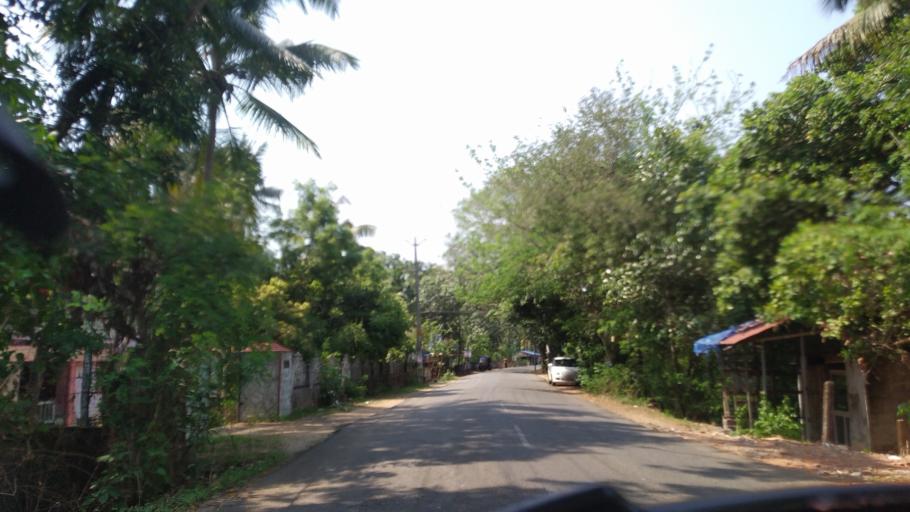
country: IN
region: Kerala
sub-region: Thrissur District
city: Kodungallur
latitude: 10.2885
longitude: 76.1356
